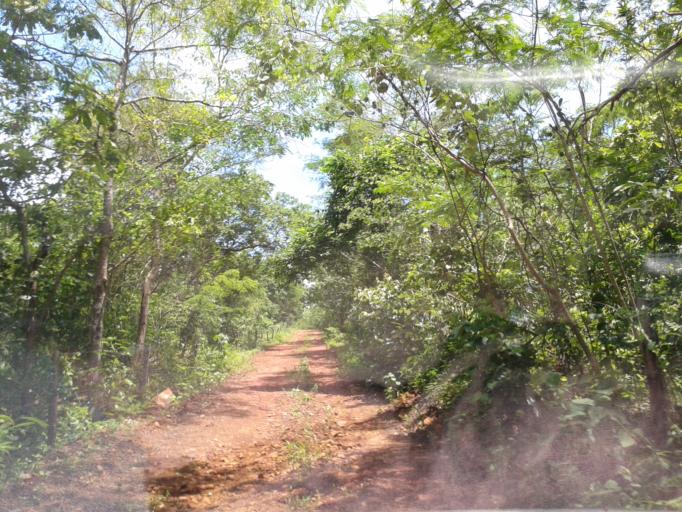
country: BR
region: Minas Gerais
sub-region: Santa Vitoria
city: Santa Vitoria
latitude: -19.1901
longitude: -50.6924
